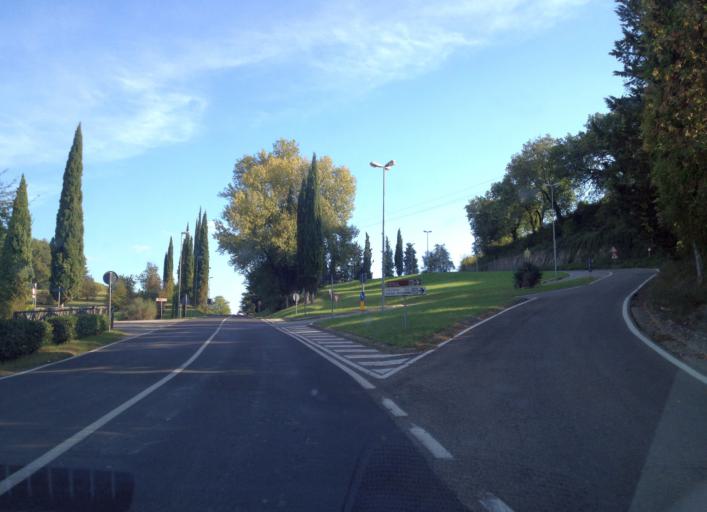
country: IT
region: Tuscany
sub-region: Provincia di Siena
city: Poggibonsi
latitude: 43.4594
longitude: 11.1478
